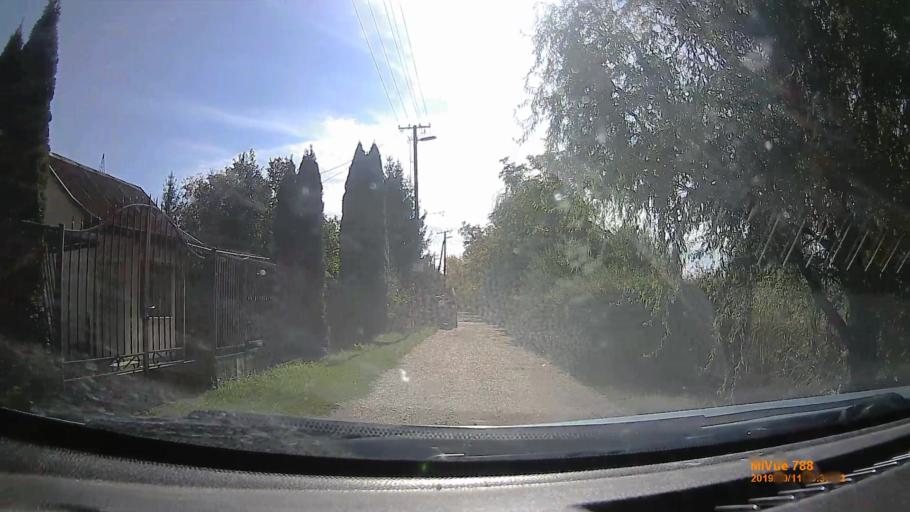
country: HU
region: Hajdu-Bihar
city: Balmazujvaros
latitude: 47.5466
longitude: 21.3297
